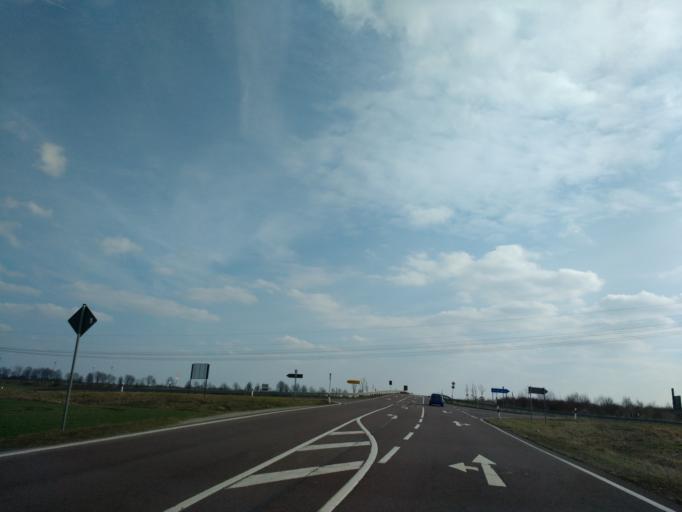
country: DE
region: Saxony-Anhalt
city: Schraplau
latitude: 51.4210
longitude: 11.6485
